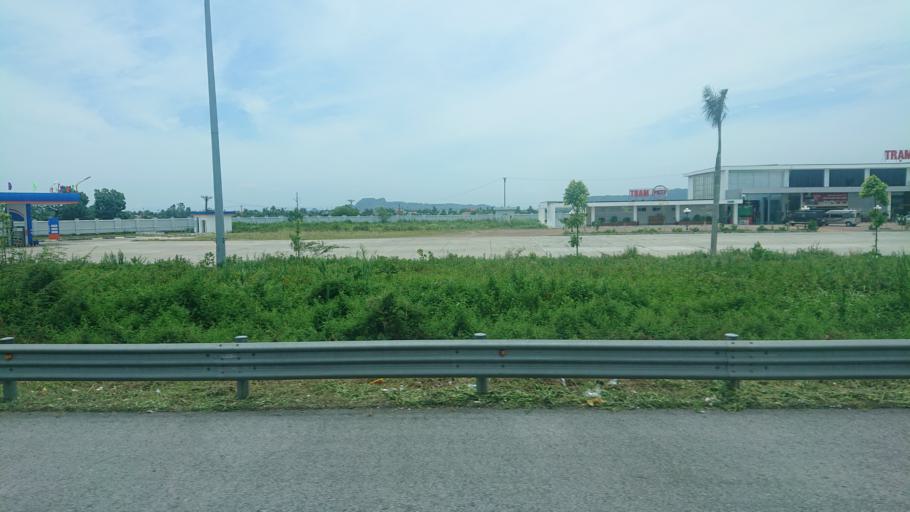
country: VN
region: Hai Phong
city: An Lao
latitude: 20.7938
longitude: 106.5477
